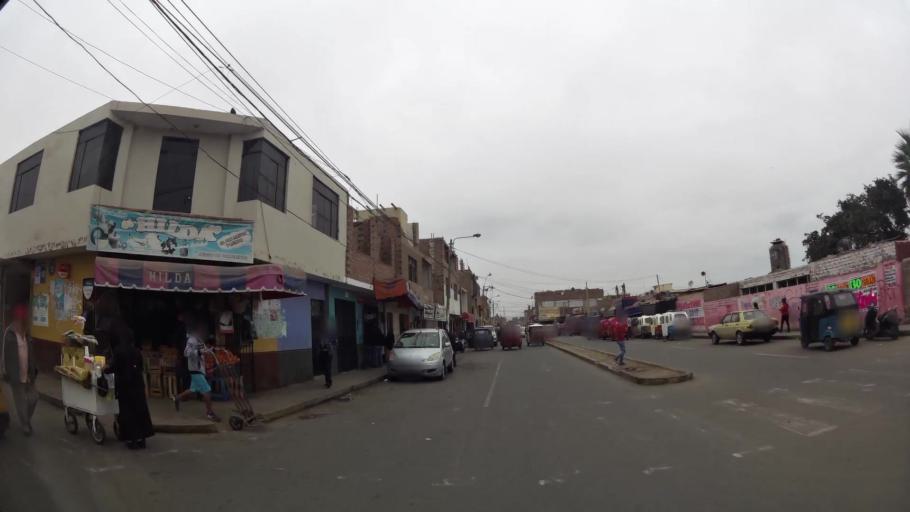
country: PE
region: Ica
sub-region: Provincia de Pisco
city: Pisco
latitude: -13.7126
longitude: -76.2067
